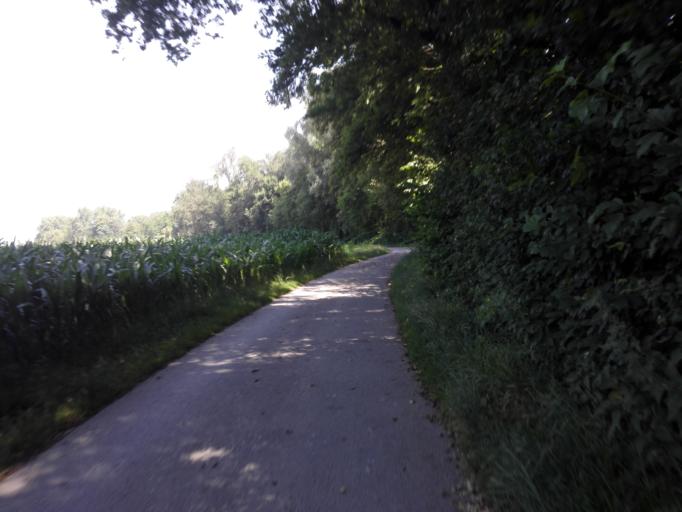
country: AT
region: Styria
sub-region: Politischer Bezirk Graz-Umgebung
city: Gossendorf
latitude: 46.9818
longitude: 15.4719
